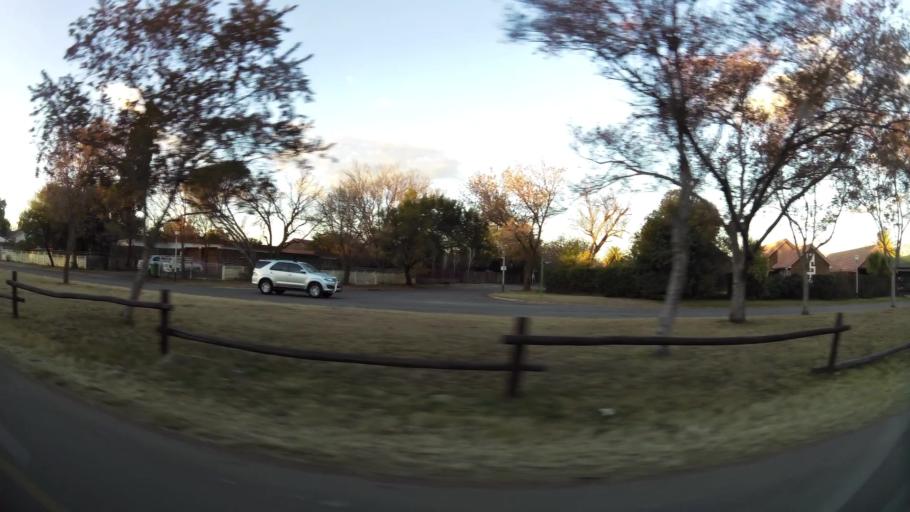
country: ZA
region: North-West
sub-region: Dr Kenneth Kaunda District Municipality
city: Potchefstroom
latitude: -26.7213
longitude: 27.1150
